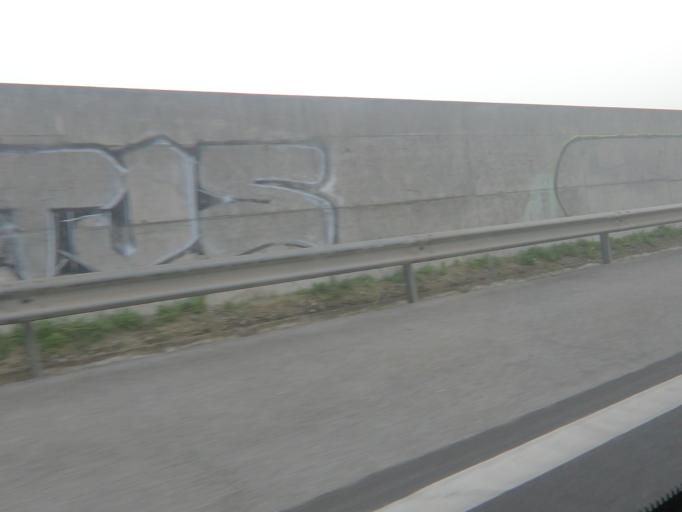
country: PT
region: Setubal
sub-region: Montijo
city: Montijo
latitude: 38.6930
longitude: -8.9388
